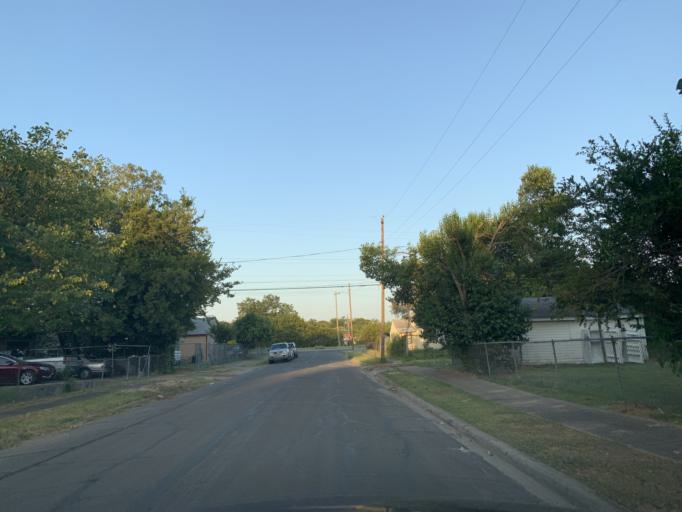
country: US
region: Texas
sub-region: Dallas County
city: Dallas
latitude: 32.7075
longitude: -96.8093
